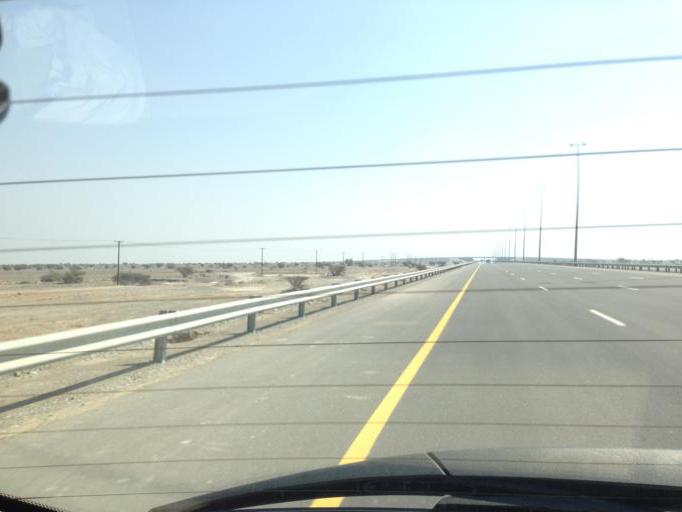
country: OM
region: Al Batinah
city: Barka'
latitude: 23.5758
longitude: 57.7563
